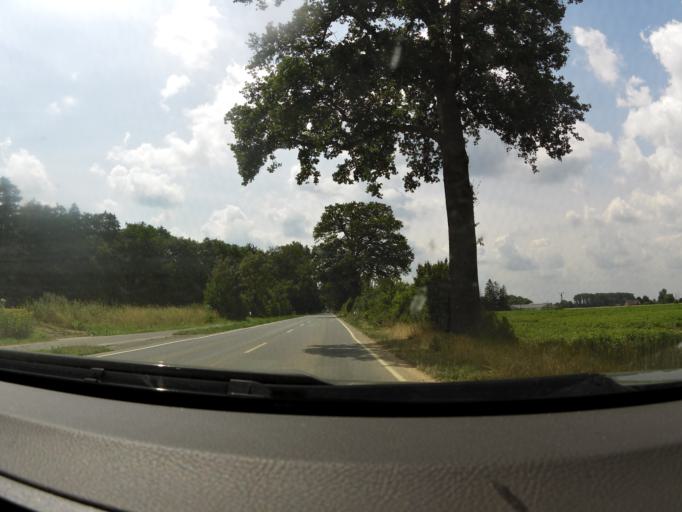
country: DE
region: North Rhine-Westphalia
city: Geldern
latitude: 51.5557
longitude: 6.3328
